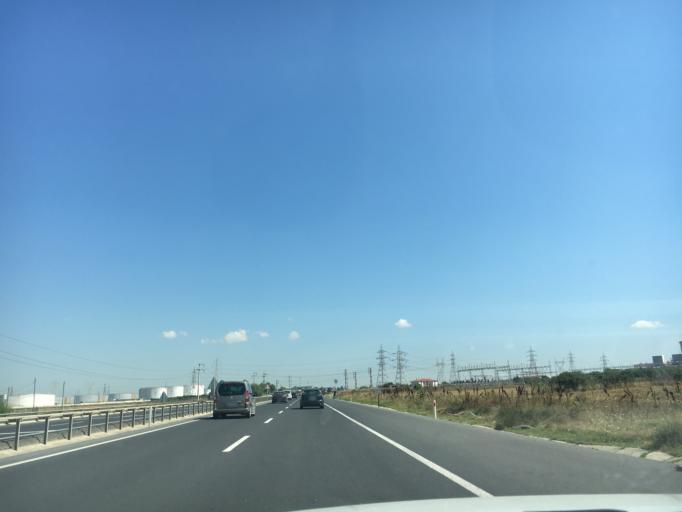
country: TR
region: Tekirdag
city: Marmara Ereglisi
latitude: 40.9906
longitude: 27.9724
